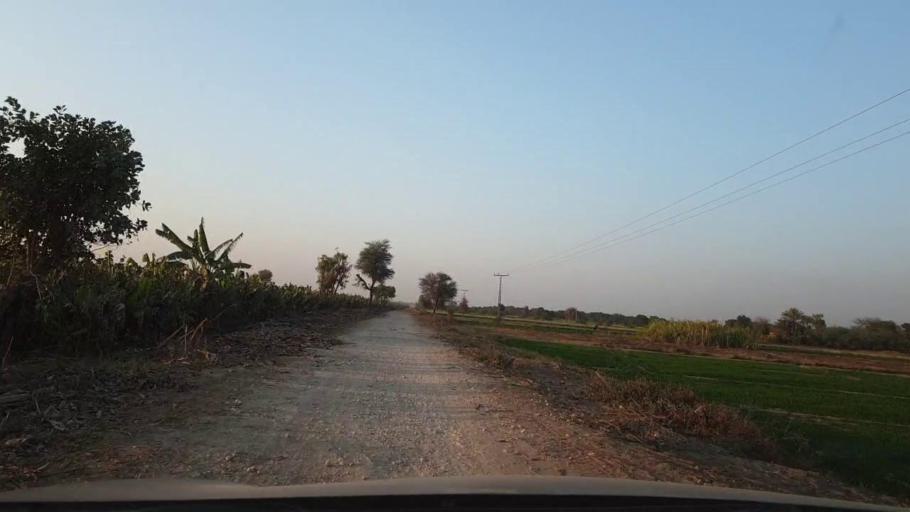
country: PK
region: Sindh
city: Tando Allahyar
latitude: 25.5151
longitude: 68.7390
